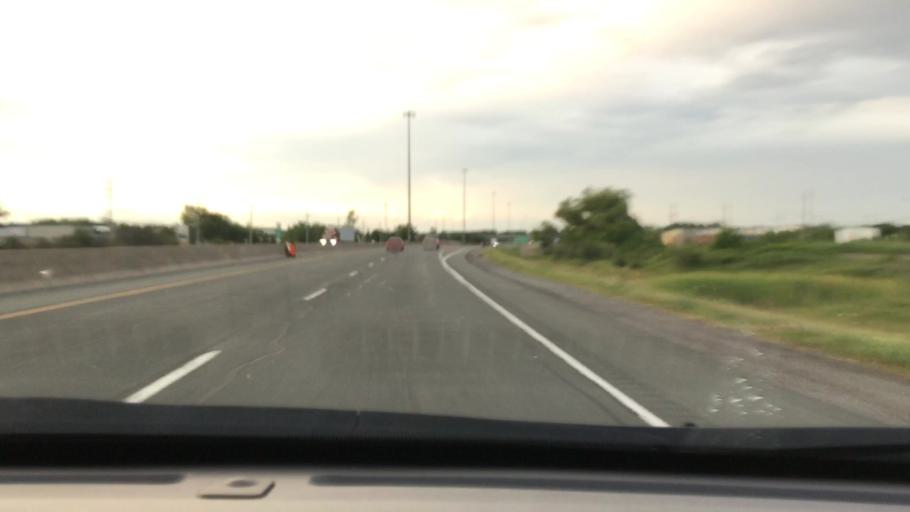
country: CA
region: Ontario
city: Niagara Falls
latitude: 43.0634
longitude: -79.1225
